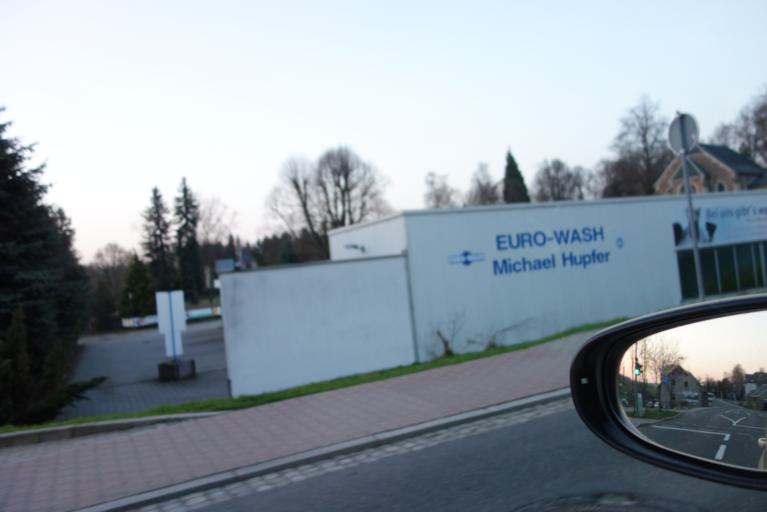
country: DE
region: Saxony
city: Marienberg
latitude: 50.6540
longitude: 13.1685
